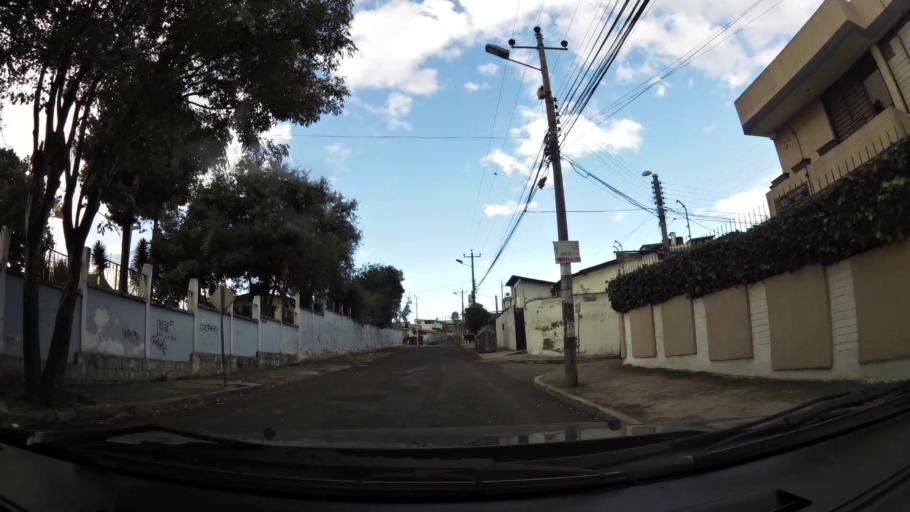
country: EC
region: Pichincha
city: Quito
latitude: -0.1398
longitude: -78.4835
